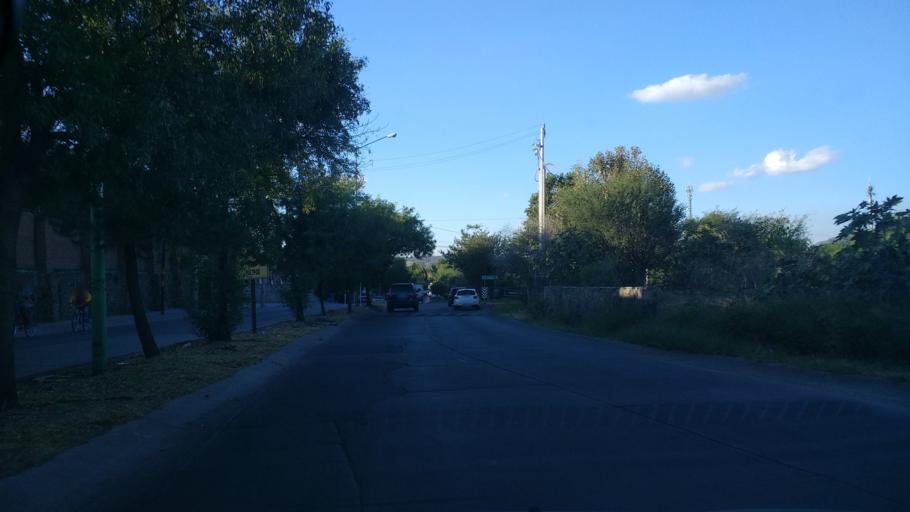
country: MX
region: Guanajuato
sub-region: Leon
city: La Ermita
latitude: 21.1805
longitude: -101.7042
